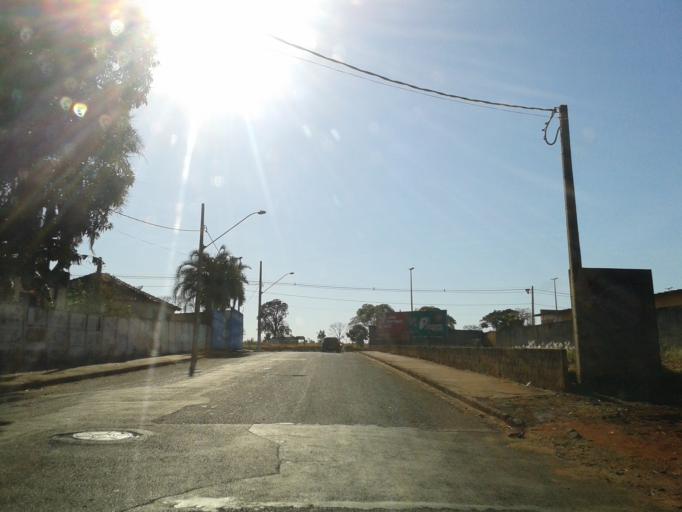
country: BR
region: Minas Gerais
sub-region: Ituiutaba
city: Ituiutaba
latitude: -18.9758
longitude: -49.4415
